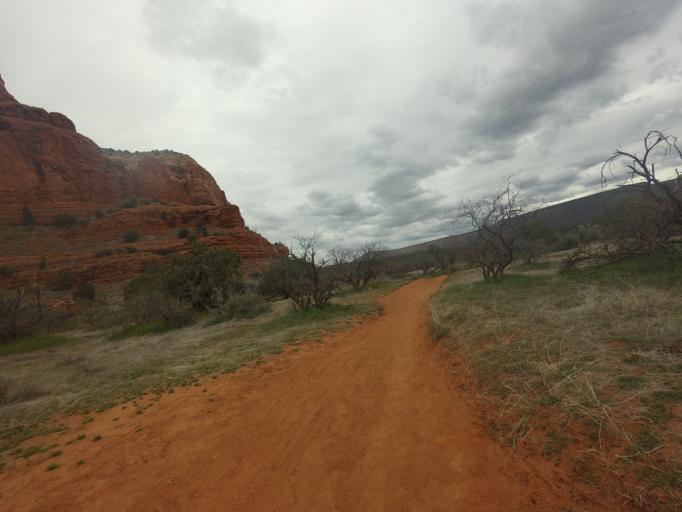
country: US
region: Arizona
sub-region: Yavapai County
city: Village of Oak Creek (Big Park)
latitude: 34.7975
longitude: -111.7578
